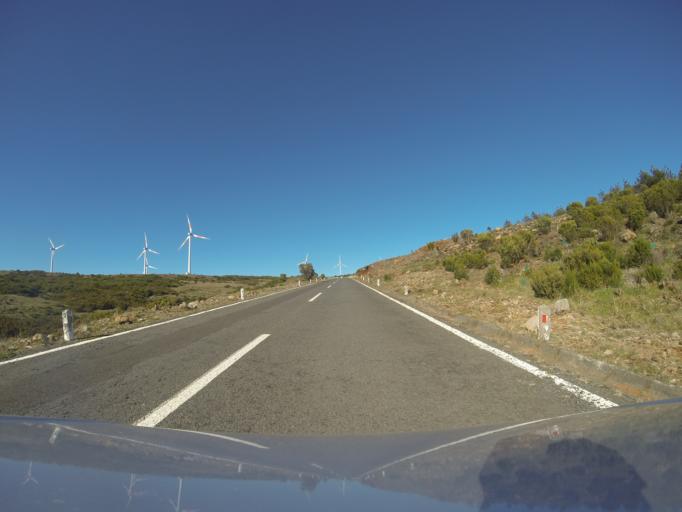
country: PT
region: Madeira
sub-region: Sao Vicente
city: Sao Vicente
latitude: 32.7425
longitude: -17.0570
